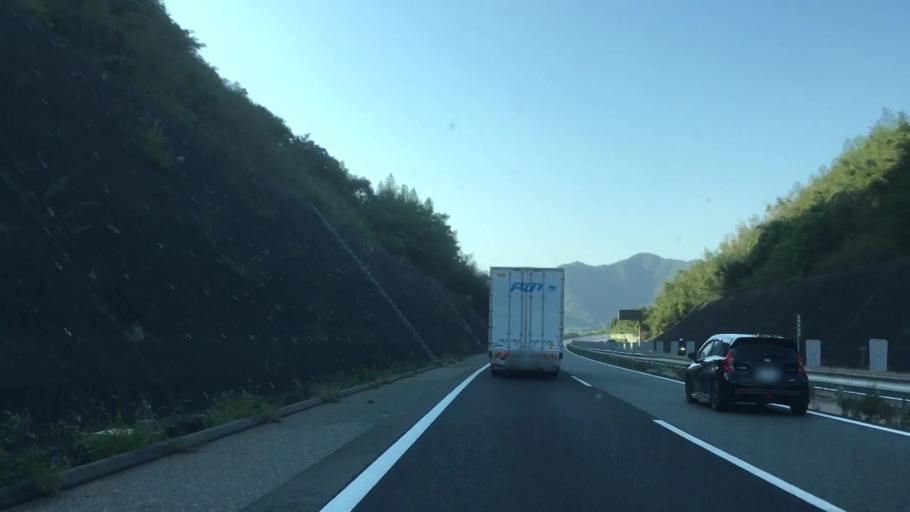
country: JP
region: Yamaguchi
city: Ogori-shimogo
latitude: 34.0902
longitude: 131.4593
